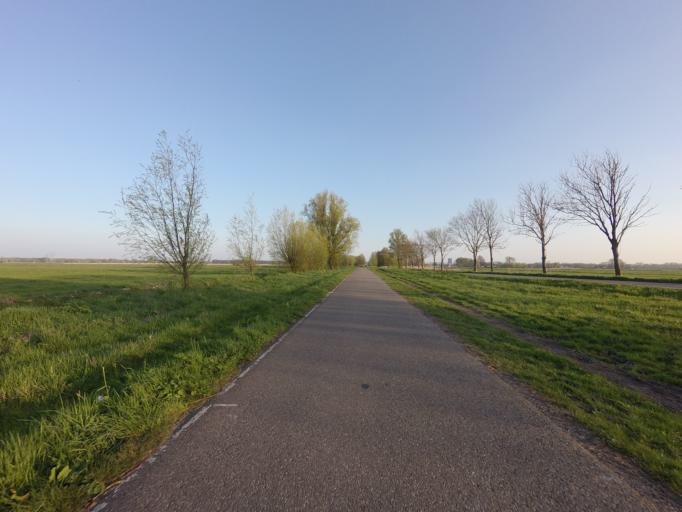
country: NL
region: South Holland
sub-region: Gemeente Schiedam
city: Schiedam
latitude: 51.9577
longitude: 4.3670
